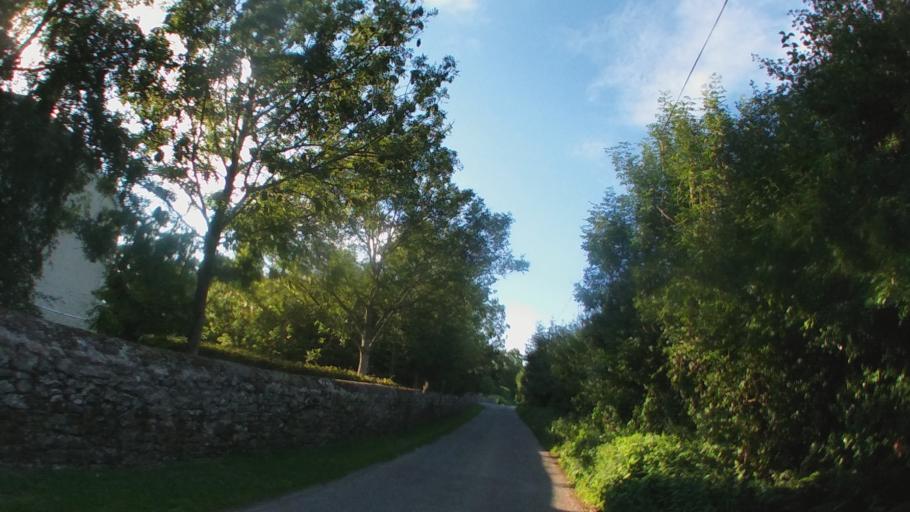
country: IE
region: Leinster
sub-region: Kilkenny
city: Kilkenny
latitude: 52.6893
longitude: -7.1879
